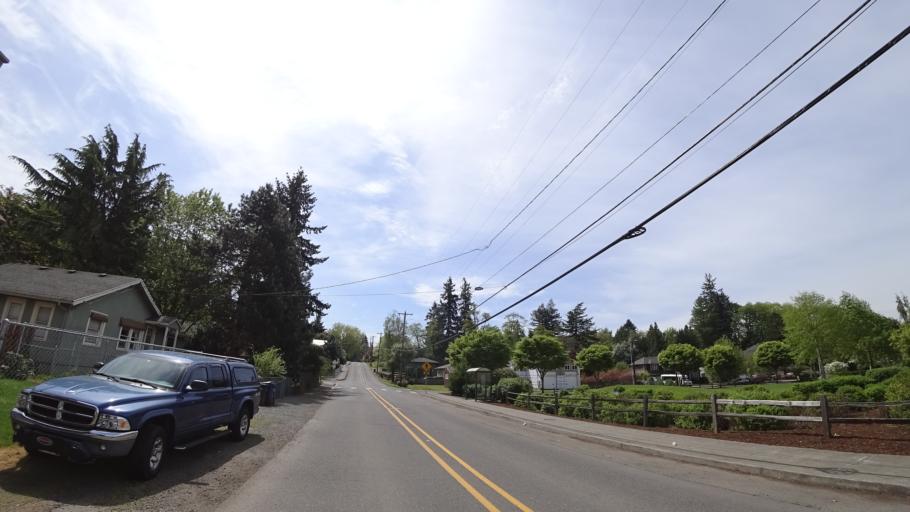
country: US
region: Oregon
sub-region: Clackamas County
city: Milwaukie
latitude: 45.4531
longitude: -122.6046
